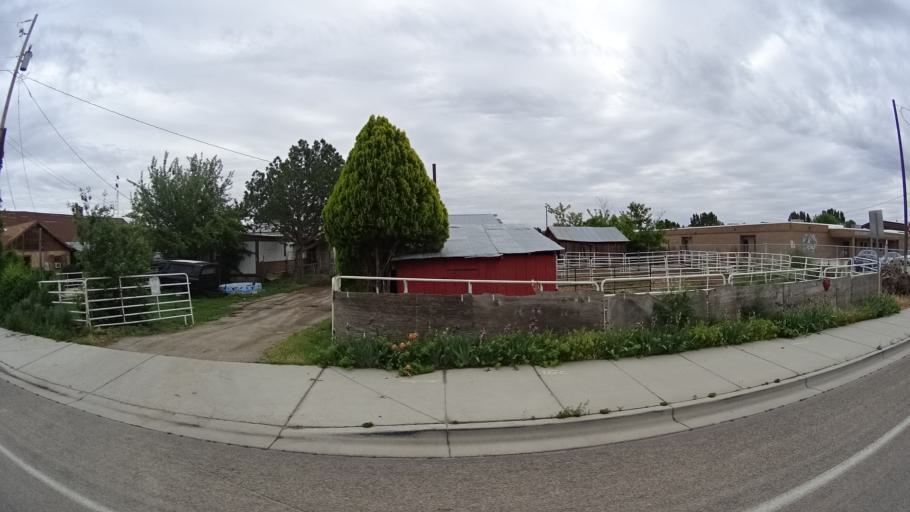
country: US
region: Idaho
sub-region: Ada County
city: Star
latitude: 43.6993
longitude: -116.4933
